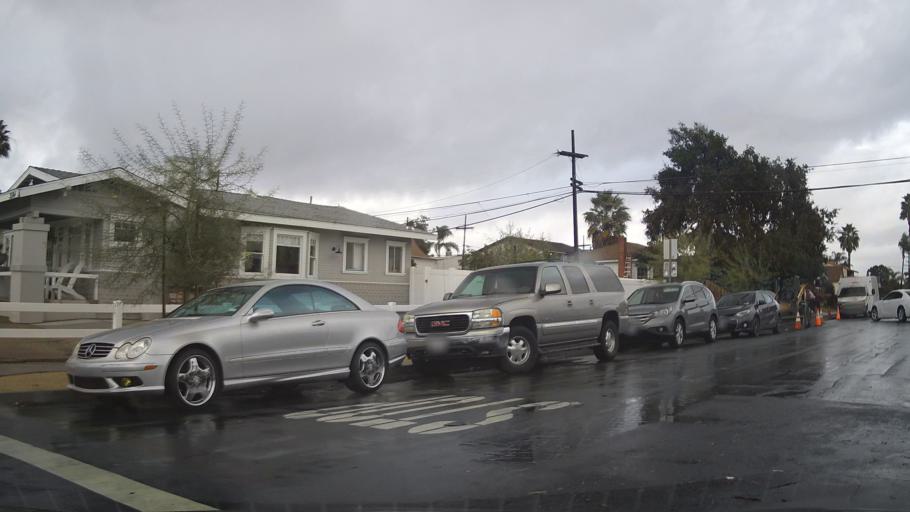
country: US
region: California
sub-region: San Diego County
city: San Diego
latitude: 32.7639
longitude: -117.1149
